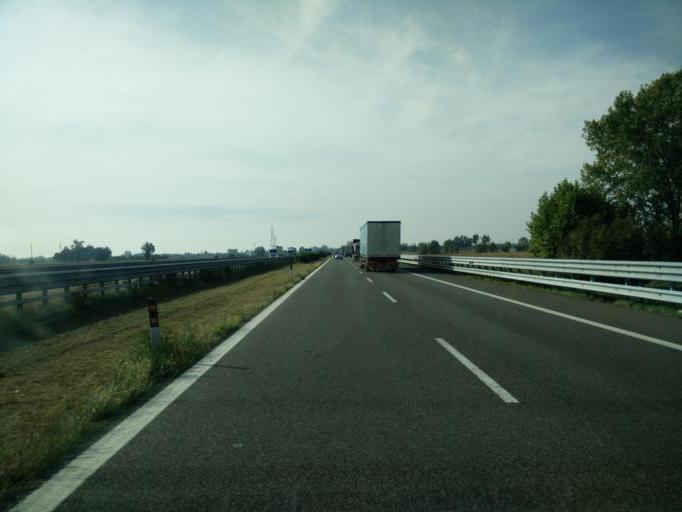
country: IT
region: Lombardy
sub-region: Provincia di Cremona
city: San Felice
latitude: 45.1621
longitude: 10.0791
